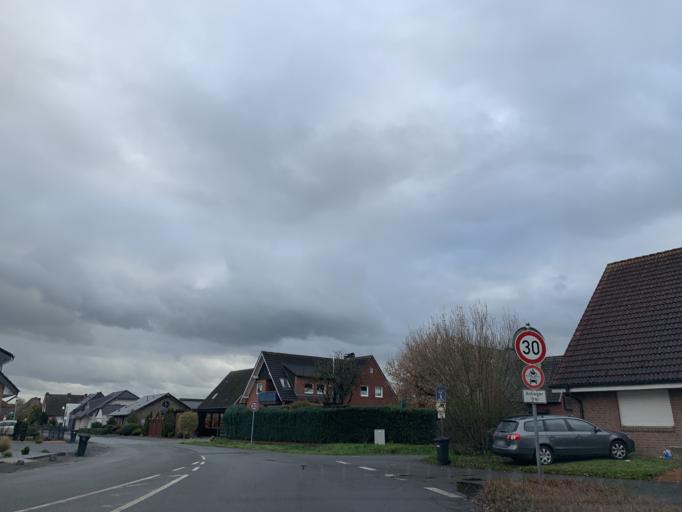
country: DE
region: North Rhine-Westphalia
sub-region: Regierungsbezirk Munster
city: Steinfurt
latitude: 52.1159
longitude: 7.3780
